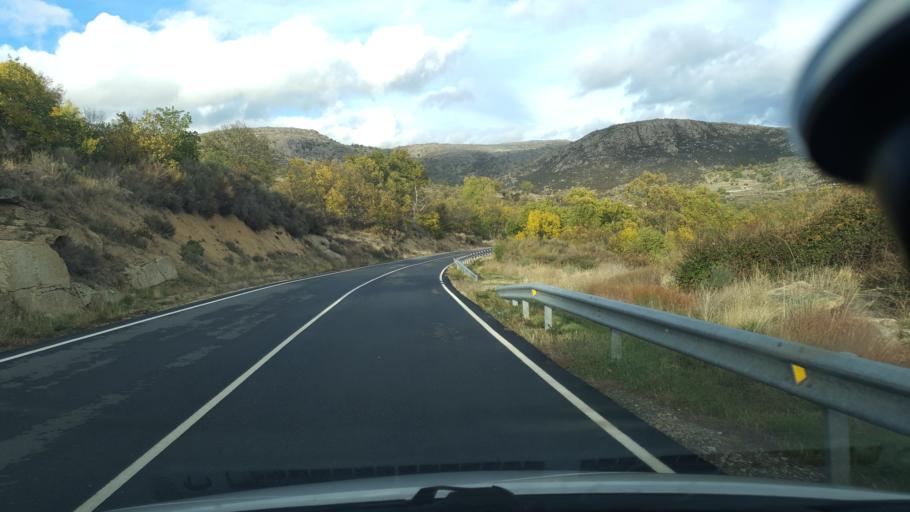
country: ES
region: Castille and Leon
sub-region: Provincia de Avila
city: Navalosa
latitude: 40.4013
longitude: -4.9057
